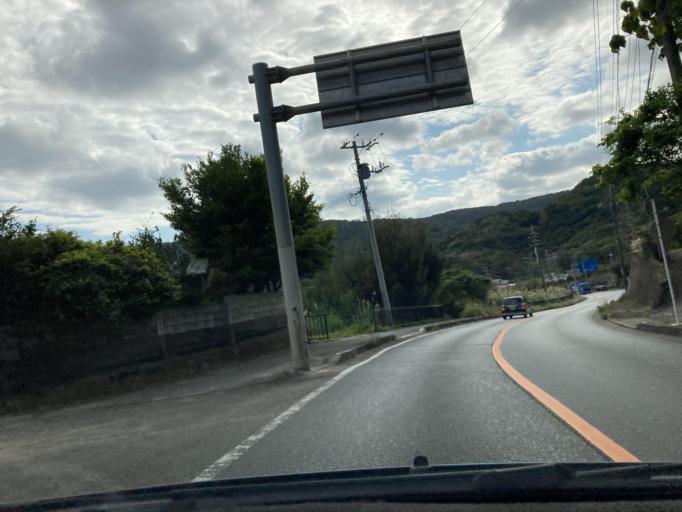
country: JP
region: Okinawa
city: Nago
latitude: 26.6547
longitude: 127.9827
